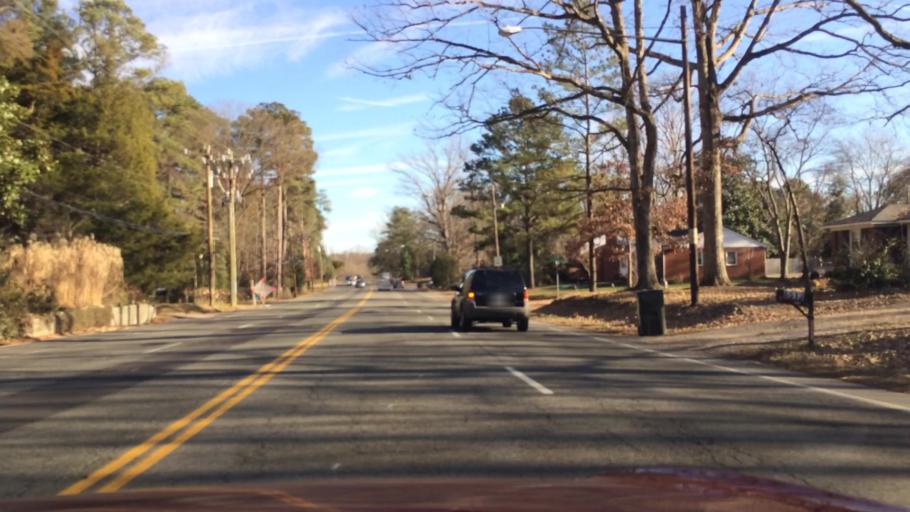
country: US
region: Virginia
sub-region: Chesterfield County
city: Bon Air
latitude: 37.5365
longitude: -77.5144
